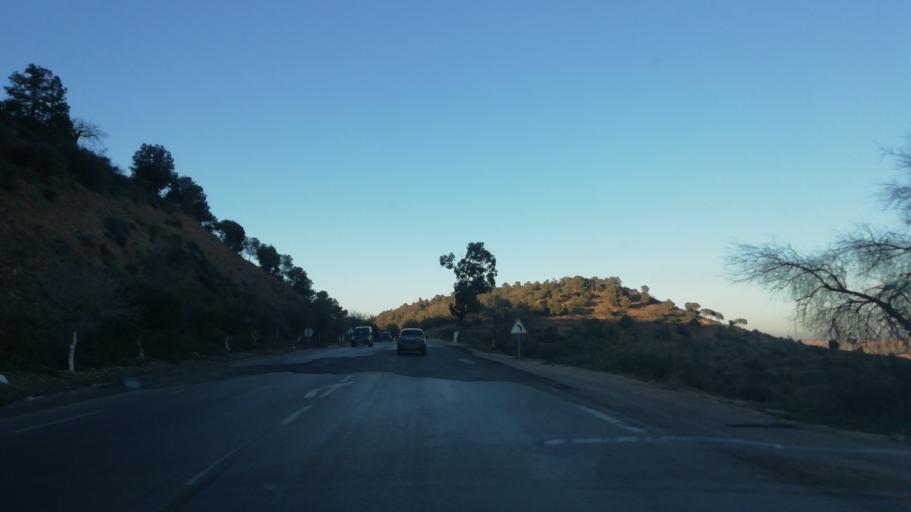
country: DZ
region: Tlemcen
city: Nedroma
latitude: 34.8736
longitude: -1.6686
